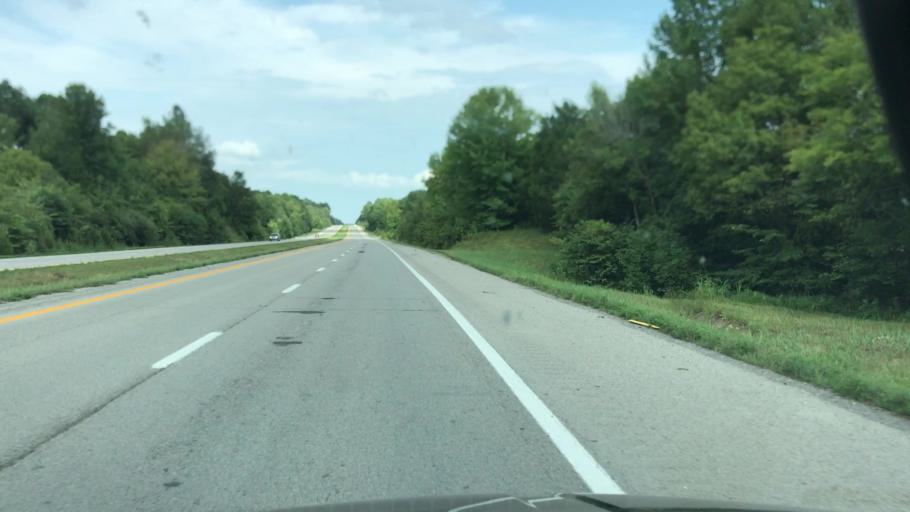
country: US
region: Kentucky
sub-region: Hopkins County
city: Nortonville
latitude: 37.2033
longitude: -87.5189
